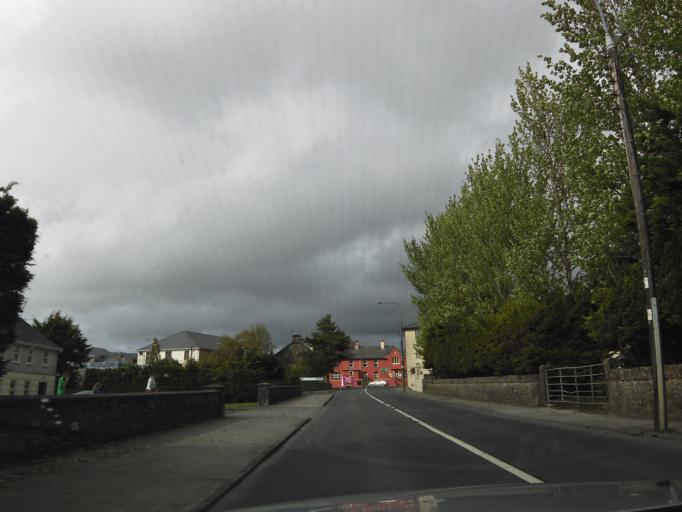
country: IE
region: Connaught
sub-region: Maigh Eo
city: Ballinrobe
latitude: 53.6196
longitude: -9.2223
